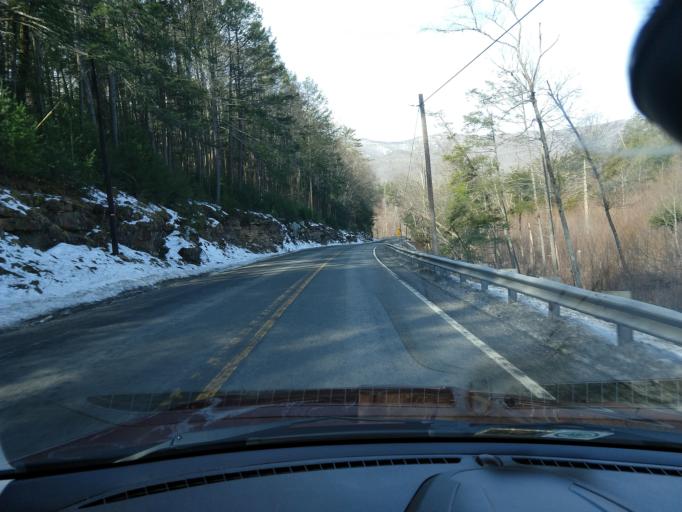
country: US
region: West Virginia
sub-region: Pocahontas County
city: Marlinton
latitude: 38.1994
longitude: -80.1281
